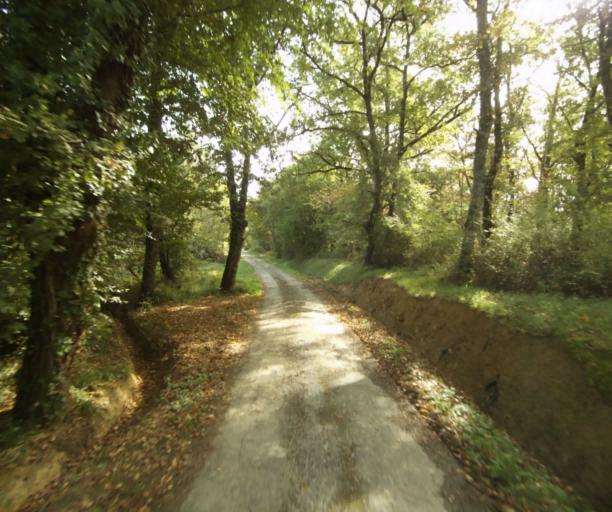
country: FR
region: Midi-Pyrenees
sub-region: Departement du Gers
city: Eauze
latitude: 43.9260
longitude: 0.0944
